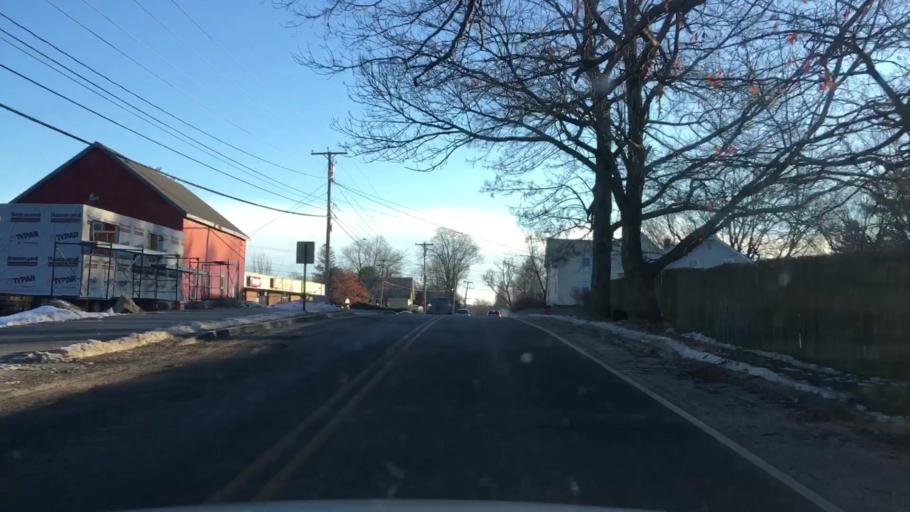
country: US
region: Maine
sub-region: Sagadahoc County
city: Bath
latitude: 43.9177
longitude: -69.8280
